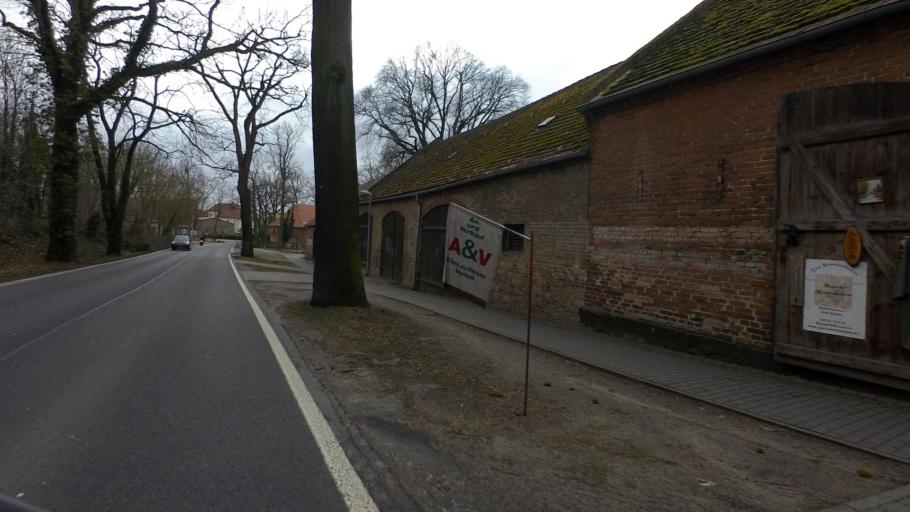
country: DE
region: Brandenburg
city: Trebbin
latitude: 52.2198
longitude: 13.2180
